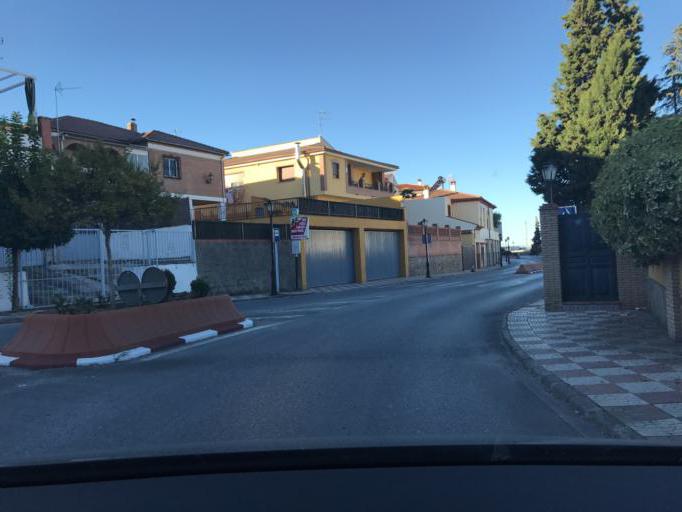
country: ES
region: Andalusia
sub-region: Provincia de Granada
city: Alfacar
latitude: 37.2352
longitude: -3.5659
